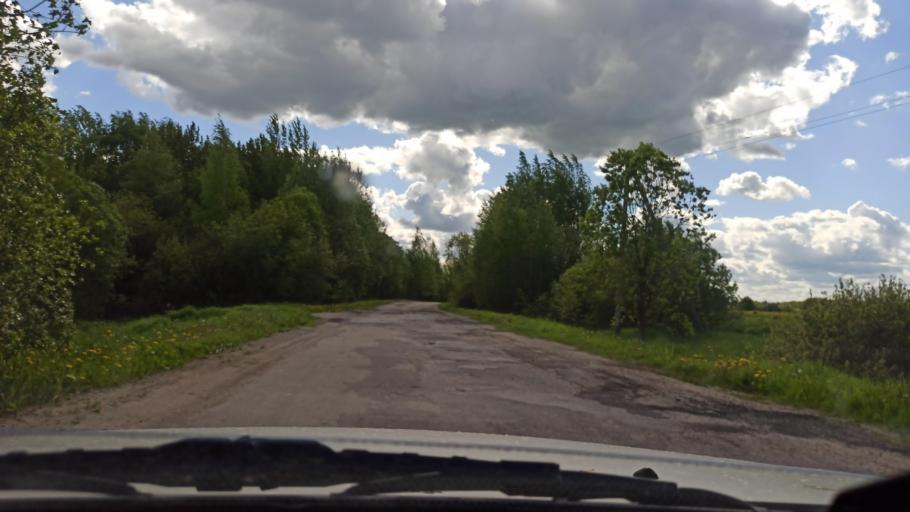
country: RU
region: Vologda
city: Molochnoye
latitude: 59.3733
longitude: 39.7052
